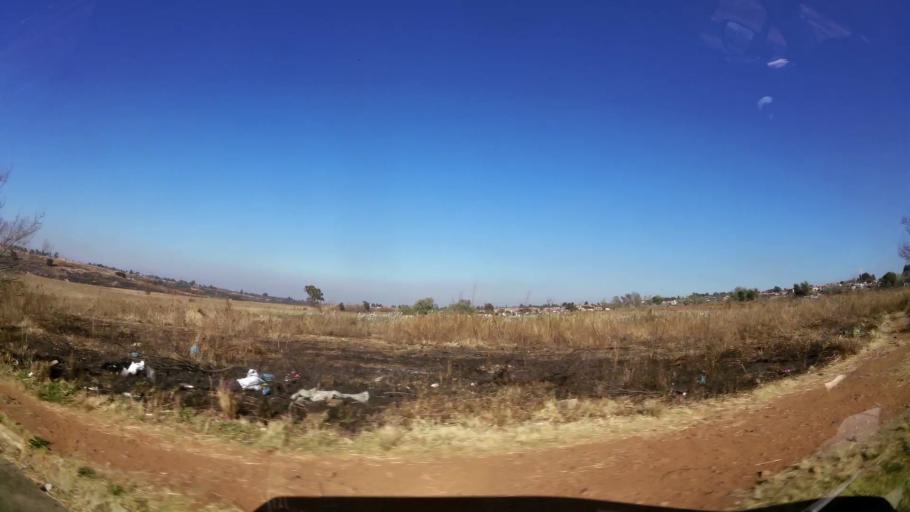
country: ZA
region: Gauteng
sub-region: City of Johannesburg Metropolitan Municipality
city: Roodepoort
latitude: -26.1538
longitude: 27.8429
